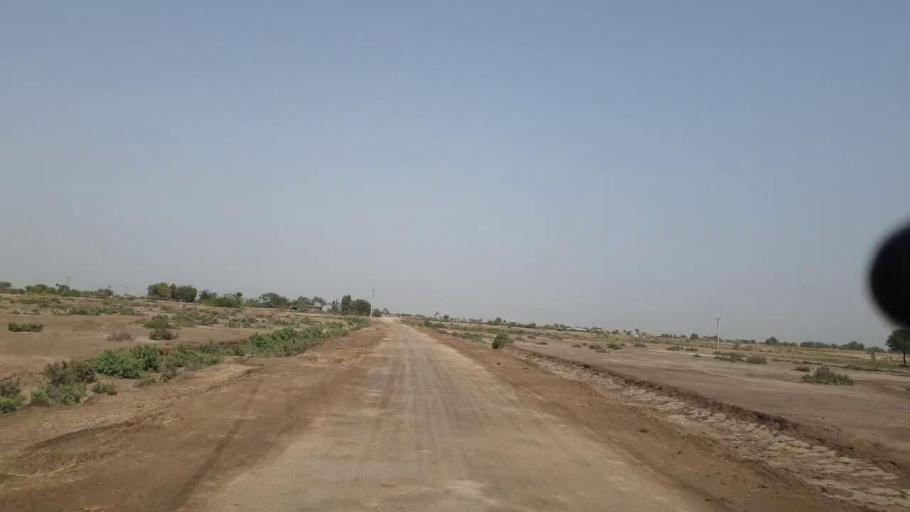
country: PK
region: Sindh
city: Matli
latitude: 25.0742
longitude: 68.6892
